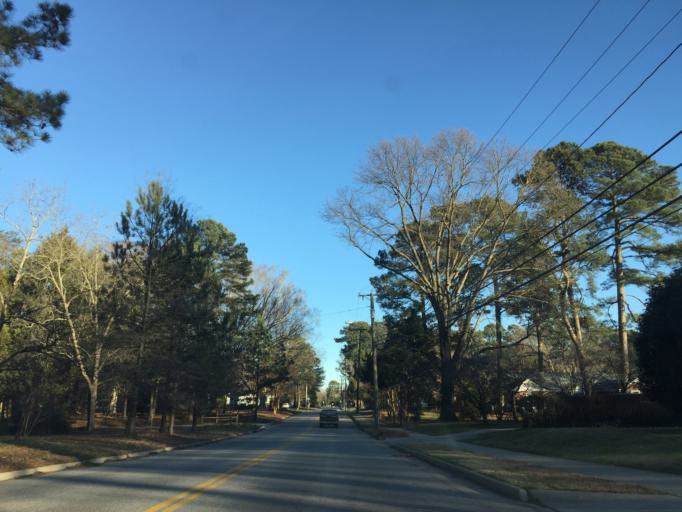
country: US
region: Virginia
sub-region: City of Newport News
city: Newport News
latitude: 37.0773
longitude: -76.5140
